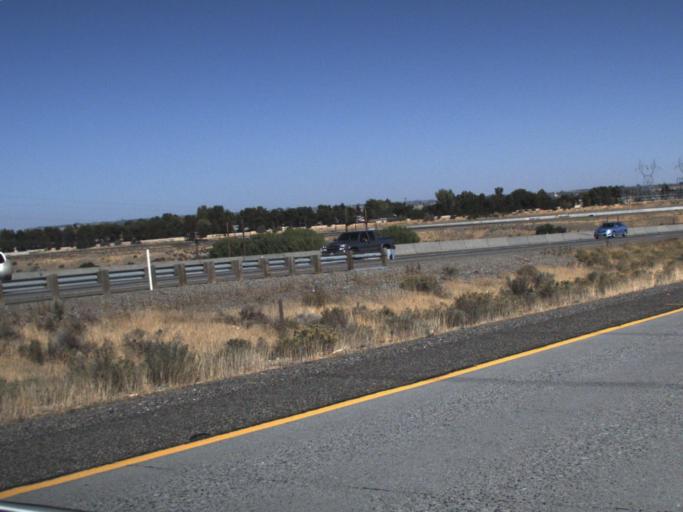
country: US
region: Washington
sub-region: Benton County
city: Richland
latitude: 46.2564
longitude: -119.2978
